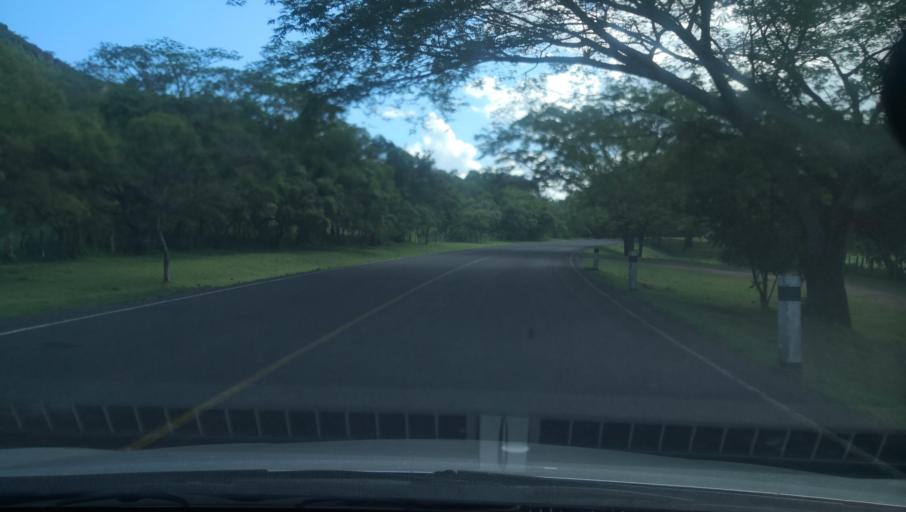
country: NI
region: Madriz
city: Somoto
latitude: 13.4650
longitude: -86.6378
